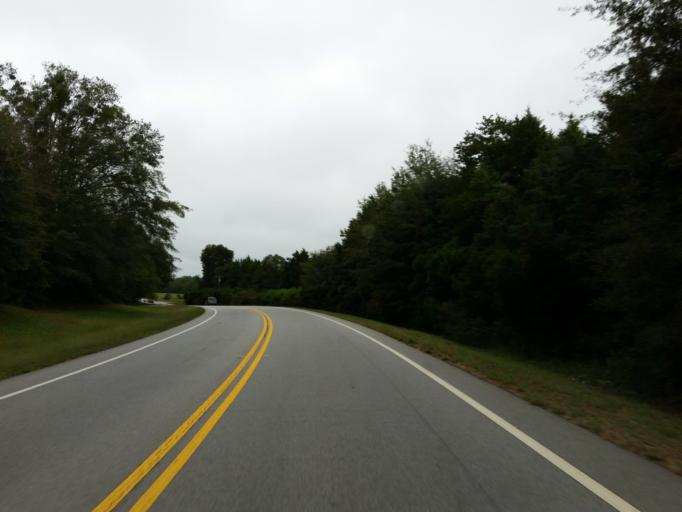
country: US
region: Georgia
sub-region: Lamar County
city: Barnesville
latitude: 32.9926
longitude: -84.1226
